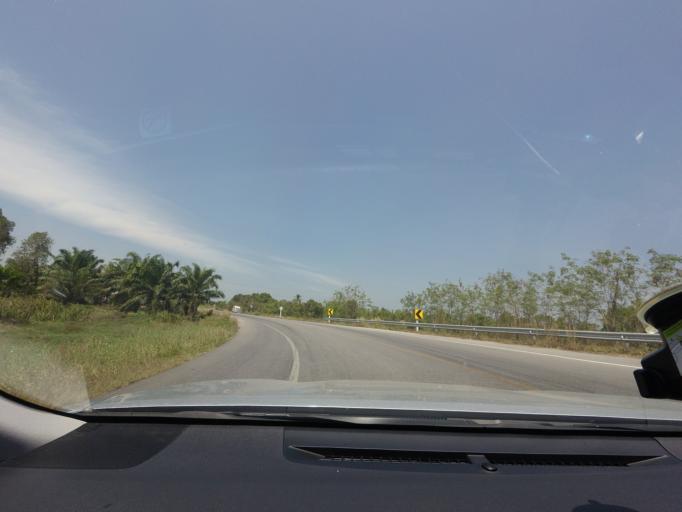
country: TH
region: Surat Thani
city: Tha Chang
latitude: 9.2149
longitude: 99.1895
